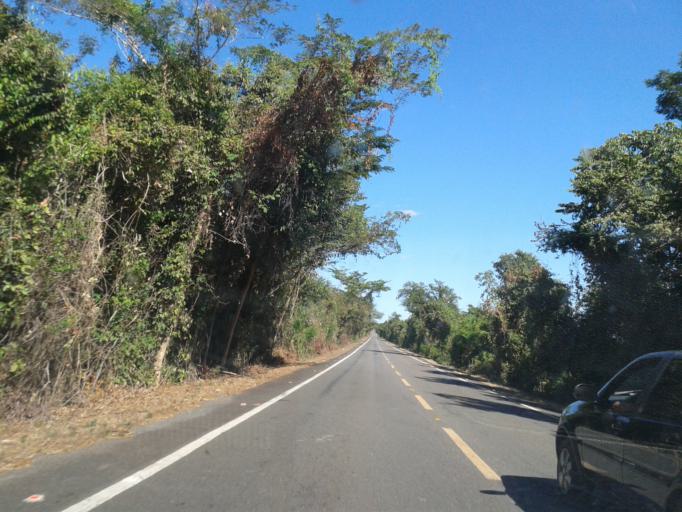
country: BR
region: Goias
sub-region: Sao Miguel Do Araguaia
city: Sao Miguel do Araguaia
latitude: -13.8727
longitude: -50.3319
